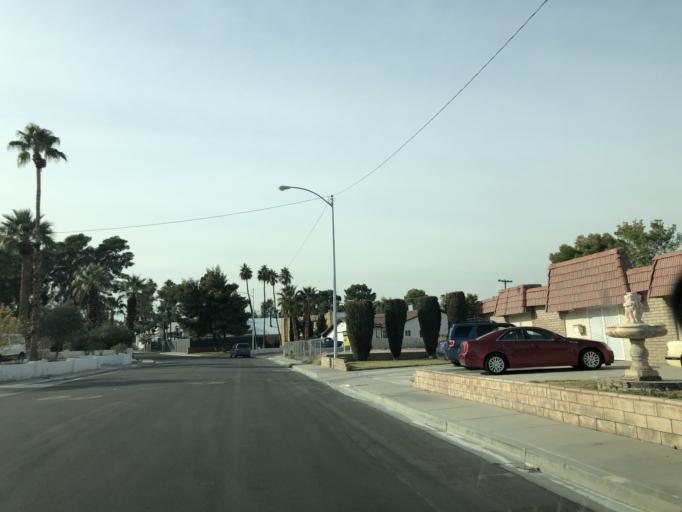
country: US
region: Nevada
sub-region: Clark County
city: Winchester
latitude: 36.1198
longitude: -115.1226
